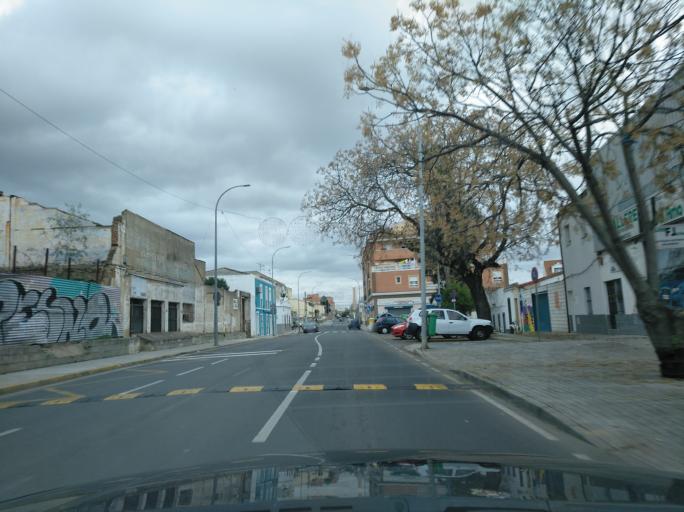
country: ES
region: Extremadura
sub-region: Provincia de Badajoz
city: Badajoz
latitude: 38.8930
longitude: -6.9812
